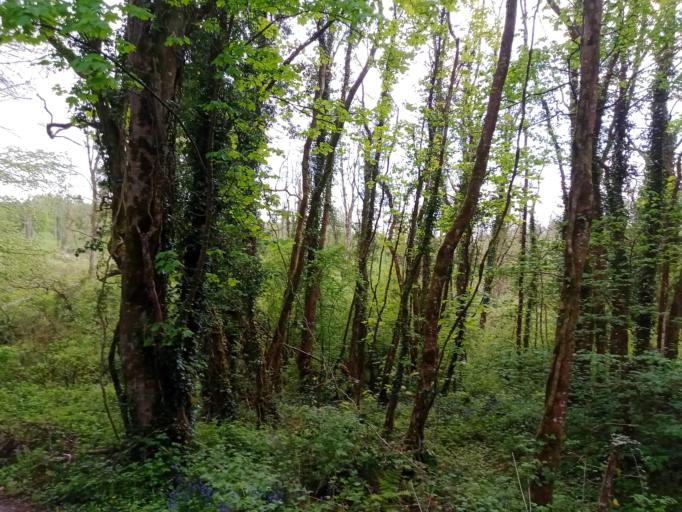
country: IE
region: Leinster
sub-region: Kilkenny
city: Castlecomer
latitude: 52.8172
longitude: -7.2036
